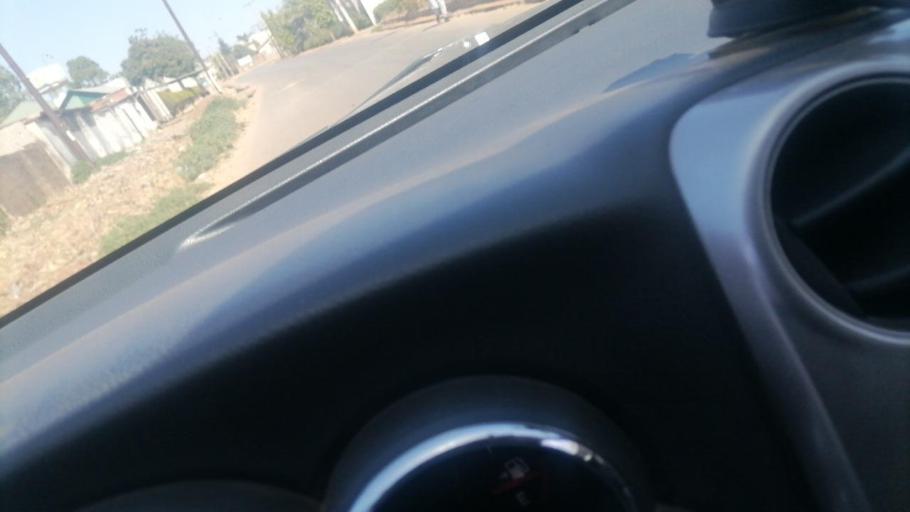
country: NG
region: Plateau
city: Jos
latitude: 9.8660
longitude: 8.9066
